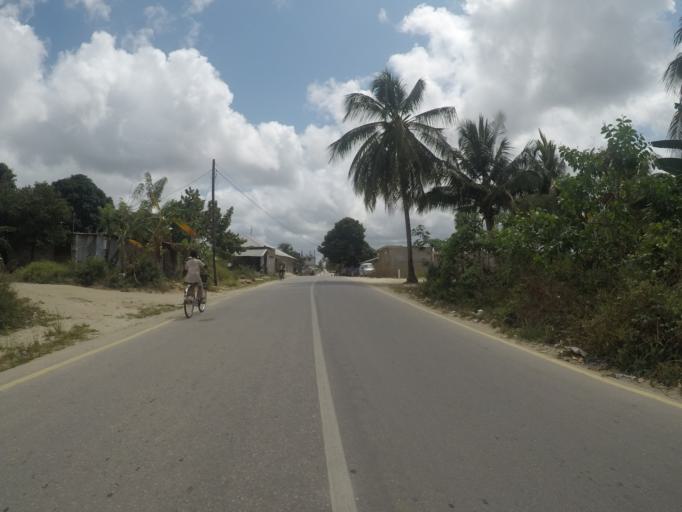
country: TZ
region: Zanzibar Urban/West
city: Zanzibar
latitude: -6.2014
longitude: 39.2434
